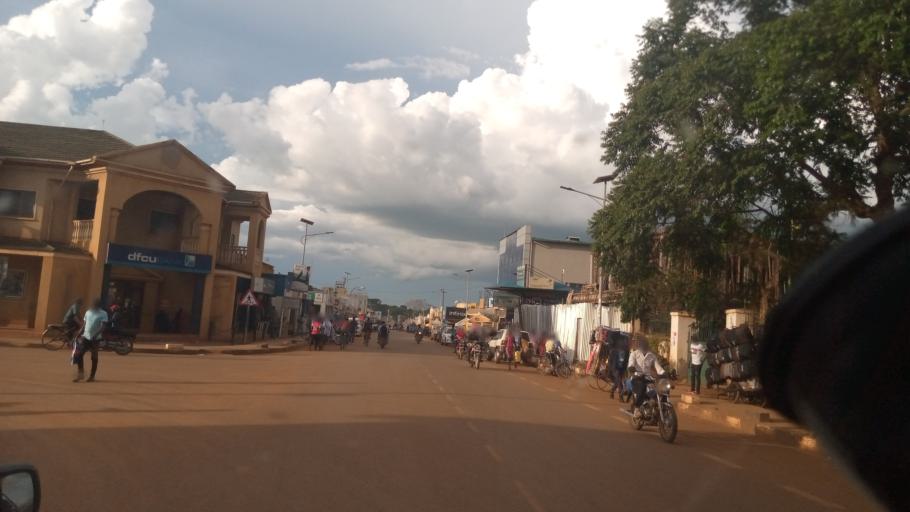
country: UG
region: Northern Region
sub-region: Lira District
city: Lira
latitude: 2.2393
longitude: 32.8947
